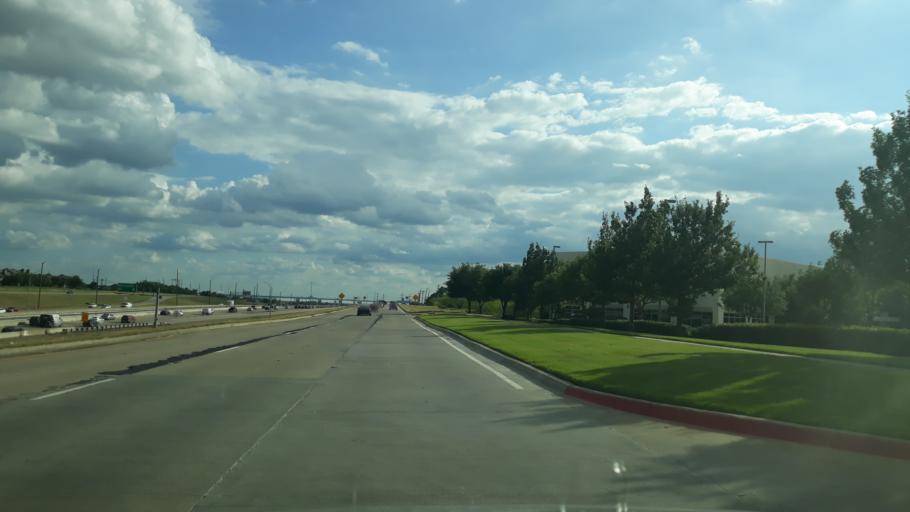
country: US
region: Texas
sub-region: Dallas County
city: Irving
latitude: 32.8653
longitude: -97.0046
